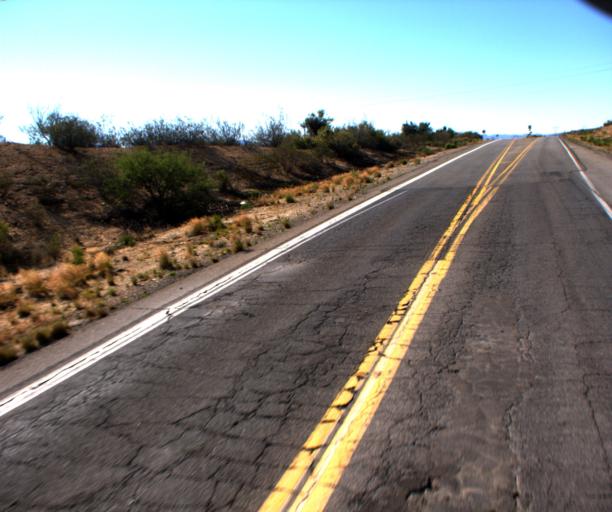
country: US
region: Arizona
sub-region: Yavapai County
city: Bagdad
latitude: 34.7680
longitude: -113.6197
